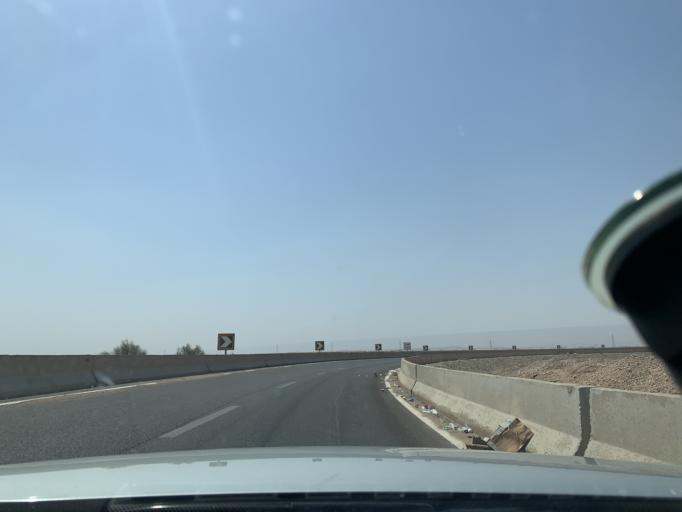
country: EG
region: As Suways
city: Ain Sukhna
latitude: 29.1056
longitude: 32.5315
